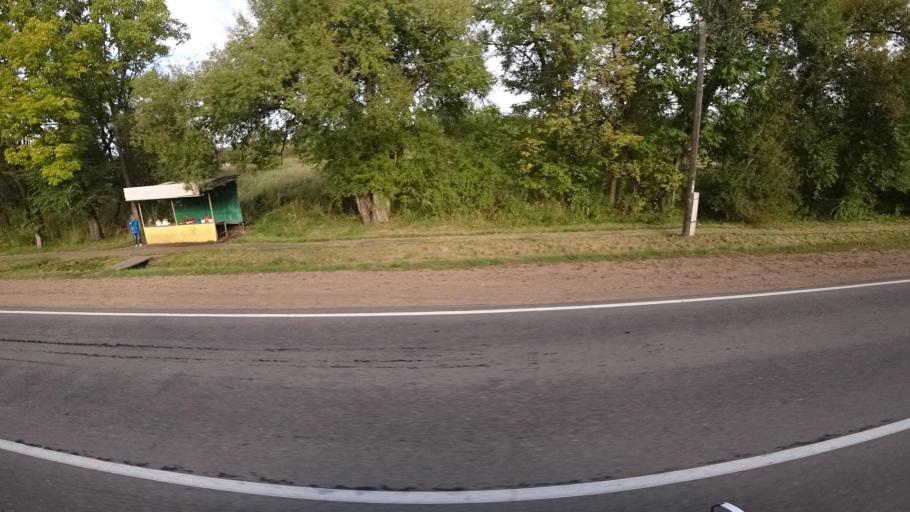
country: RU
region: Primorskiy
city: Dostoyevka
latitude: 44.2886
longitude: 133.4264
